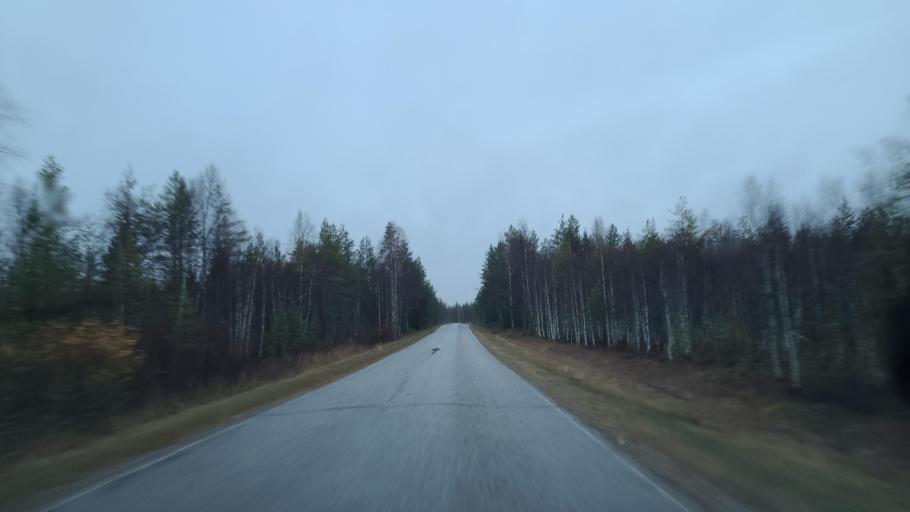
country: FI
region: Lapland
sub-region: Kemi-Tornio
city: Simo
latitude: 65.9213
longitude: 25.2003
